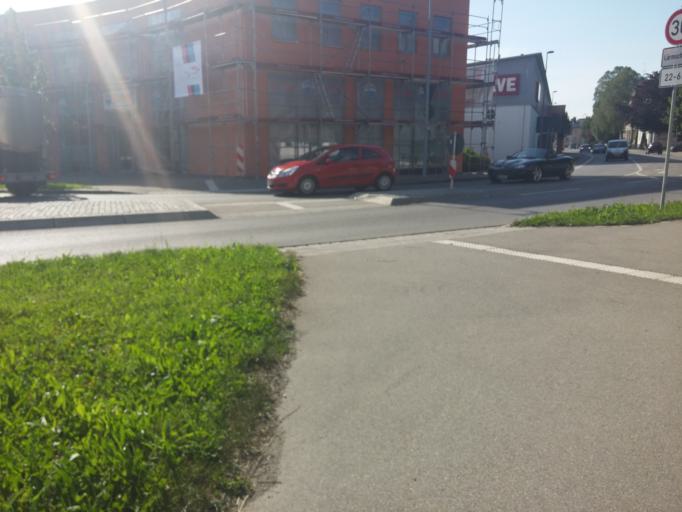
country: DE
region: Baden-Wuerttemberg
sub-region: Tuebingen Region
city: Leutkirch im Allgau
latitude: 47.8244
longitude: 10.0226
